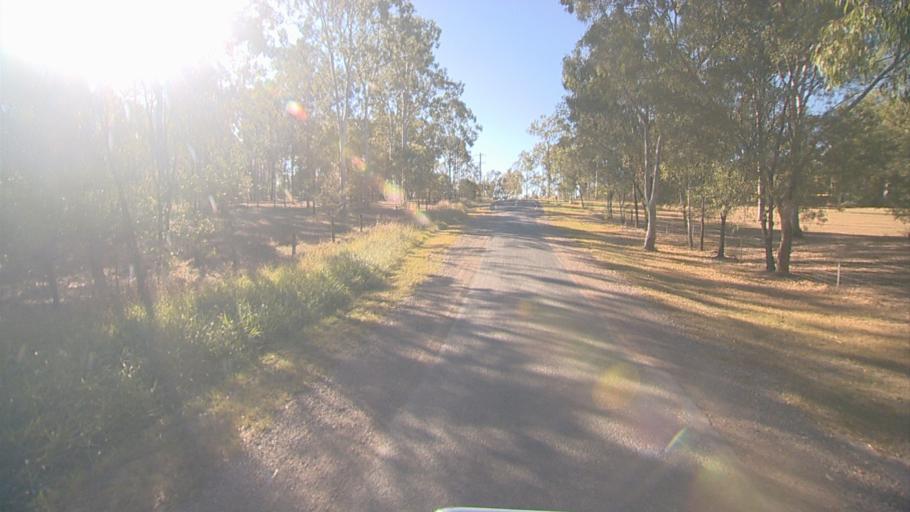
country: AU
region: Queensland
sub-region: Logan
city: North Maclean
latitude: -27.8064
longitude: 153.0340
